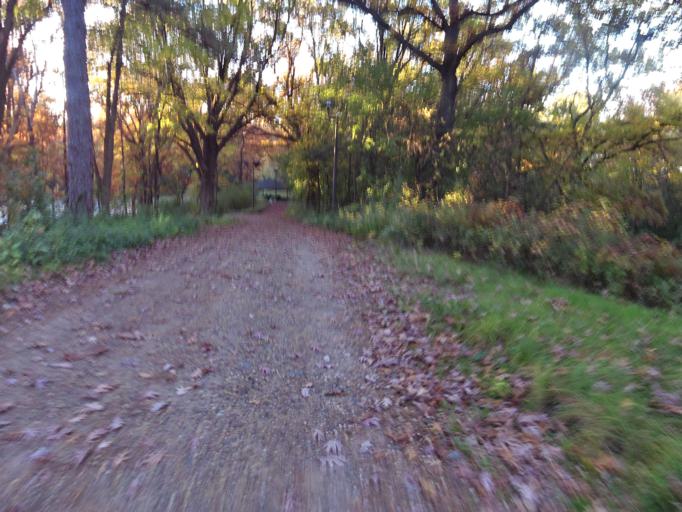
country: US
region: Minnesota
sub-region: Washington County
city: Lake Elmo
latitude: 44.9769
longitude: -92.8753
